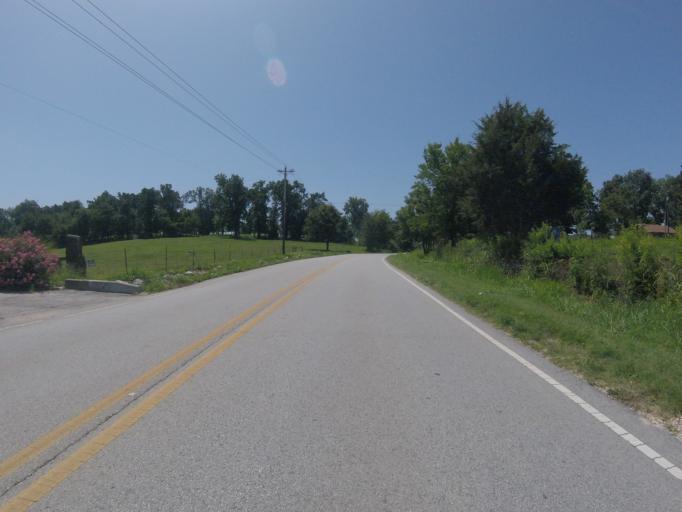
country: US
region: Arkansas
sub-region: Washington County
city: Farmington
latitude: 36.0906
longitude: -94.2150
